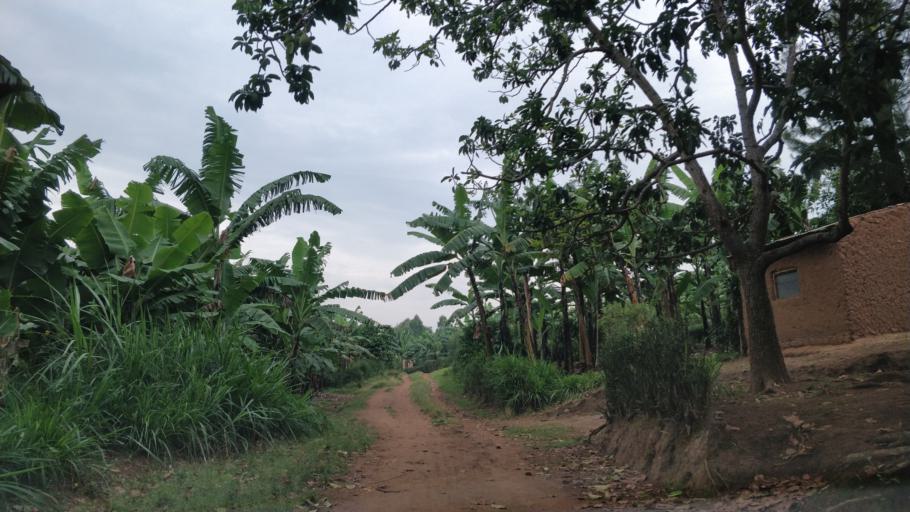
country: UG
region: Western Region
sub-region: Sheema District
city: Kibingo
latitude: -0.7016
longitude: 30.3947
